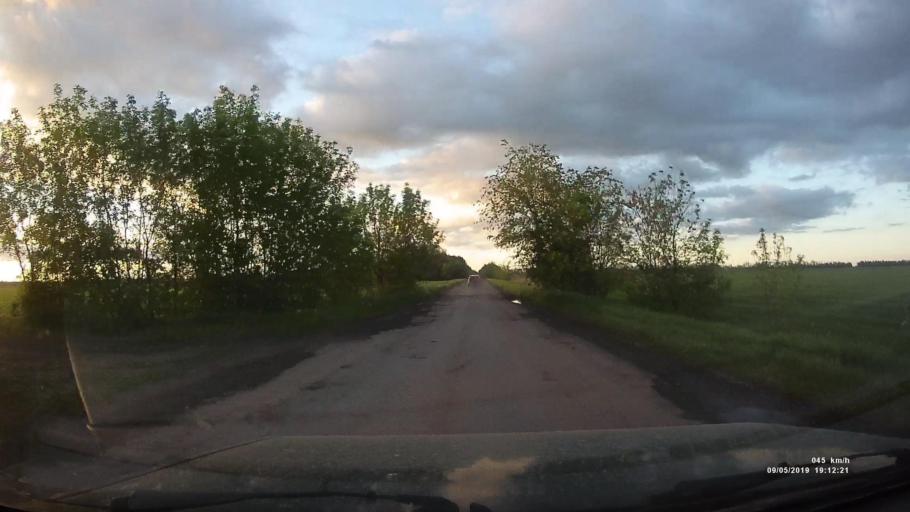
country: RU
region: Krasnodarskiy
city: Kanelovskaya
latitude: 46.7410
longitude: 39.2137
